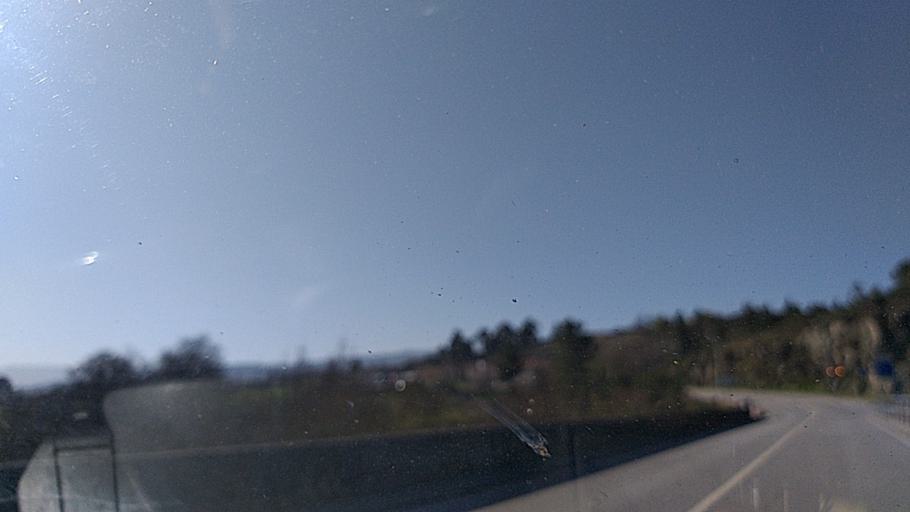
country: PT
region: Guarda
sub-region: Celorico da Beira
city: Celorico da Beira
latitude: 40.6540
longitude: -7.3830
